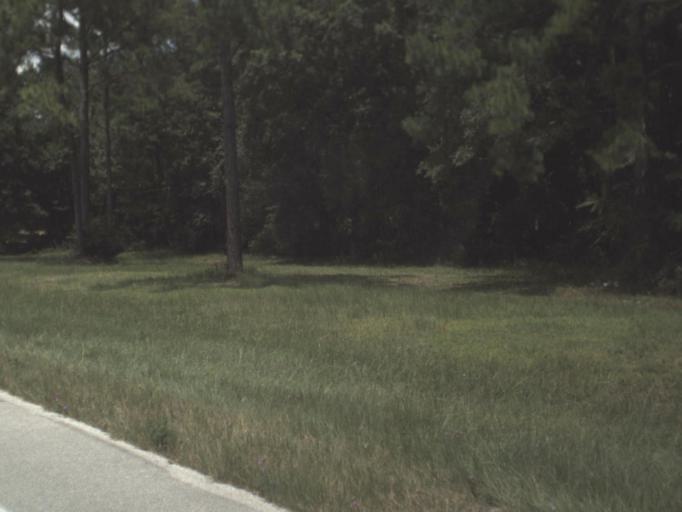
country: US
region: Florida
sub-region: Alachua County
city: Newberry
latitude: 29.7322
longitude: -82.6072
